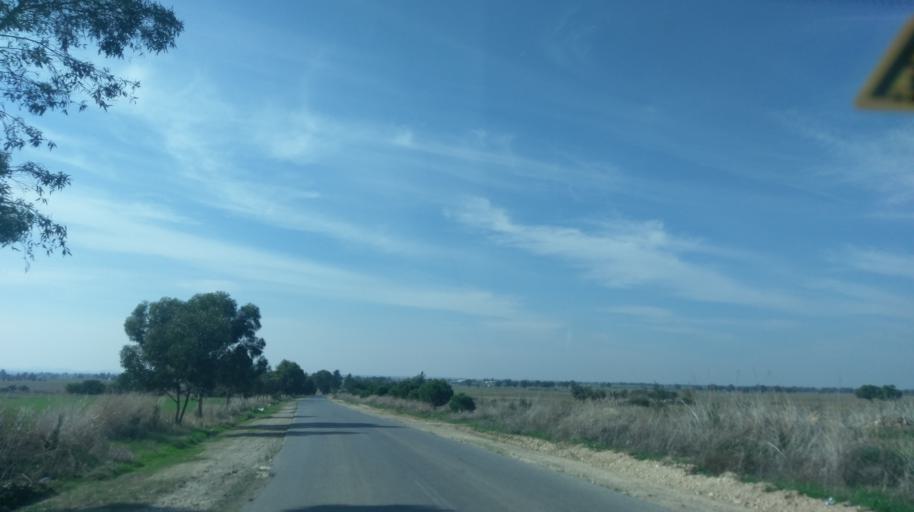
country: CY
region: Larnaka
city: Pergamos
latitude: 35.1476
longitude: 33.6754
